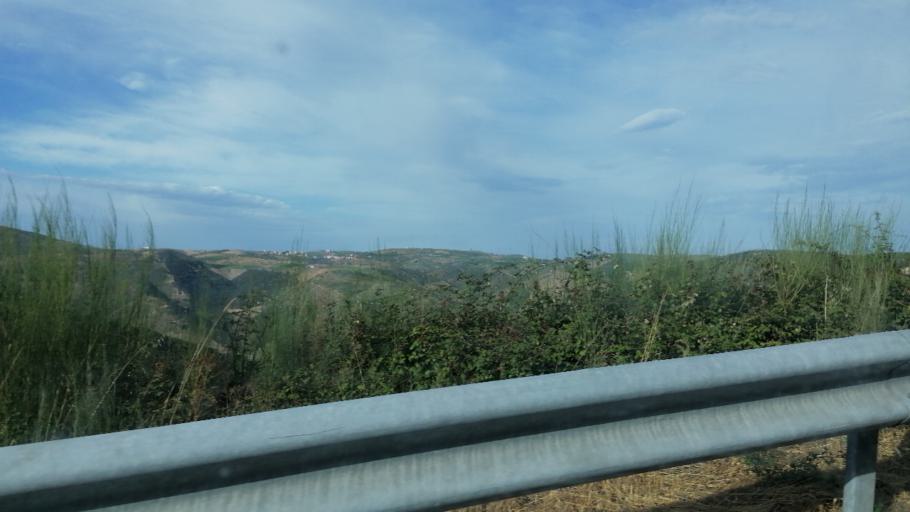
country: PT
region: Viseu
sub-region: Sao Joao da Pesqueira
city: Sao Joao da Pesqueira
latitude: 41.1076
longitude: -7.4651
